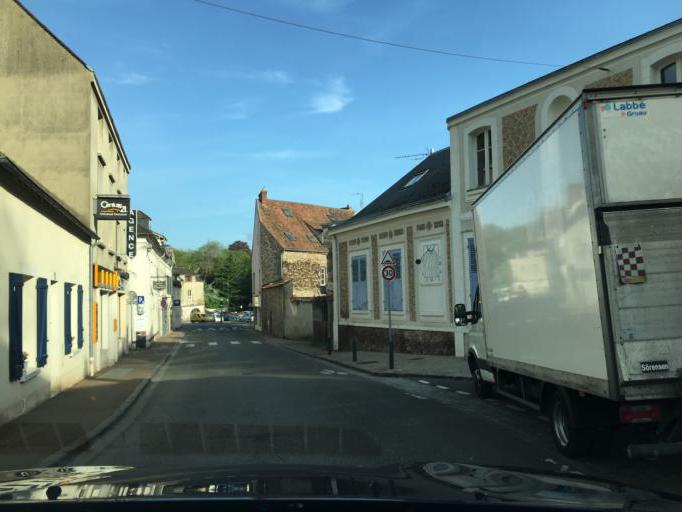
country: FR
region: Centre
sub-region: Departement d'Eure-et-Loir
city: Epernon
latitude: 48.6095
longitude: 1.6759
